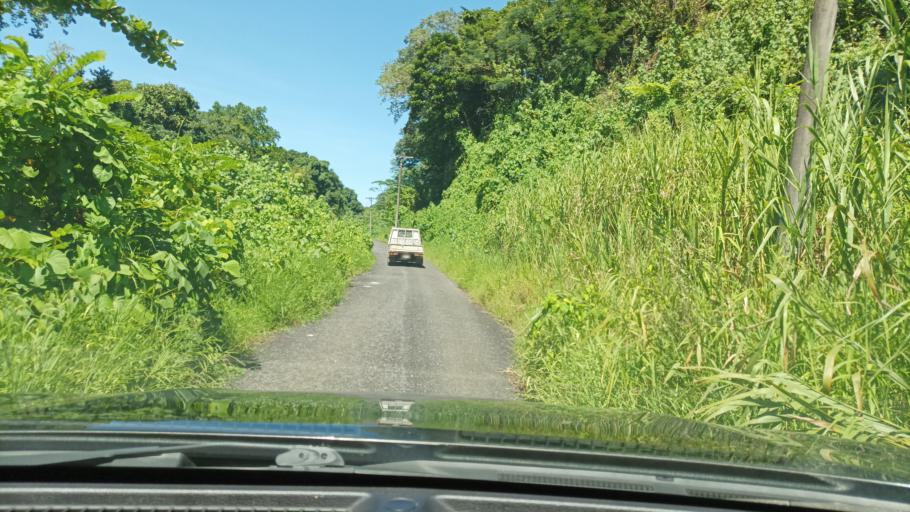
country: FM
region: Pohnpei
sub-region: Madolenihm Municipality
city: Madolenihm Municipality Government
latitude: 6.8426
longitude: 158.3100
